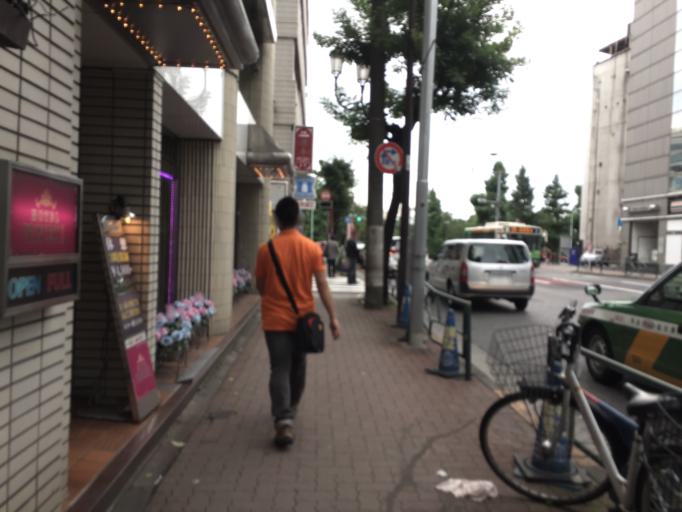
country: JP
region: Tokyo
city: Tokyo
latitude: 35.7086
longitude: 139.7698
